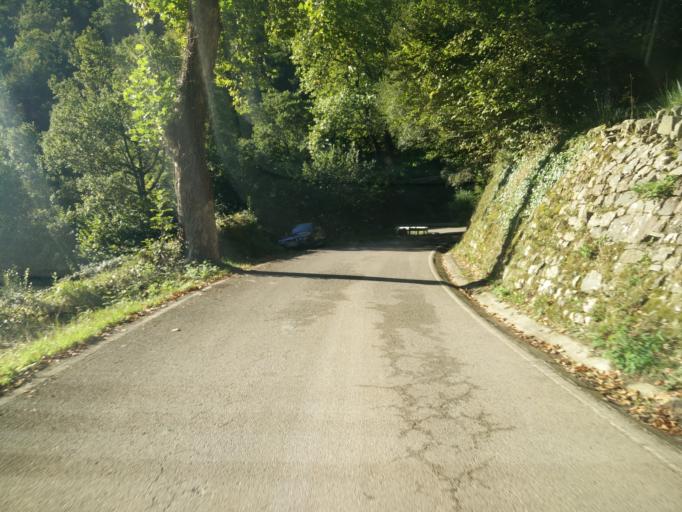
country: ES
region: Cantabria
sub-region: Provincia de Cantabria
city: San Pedro del Romeral
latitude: 43.1242
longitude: -3.8130
